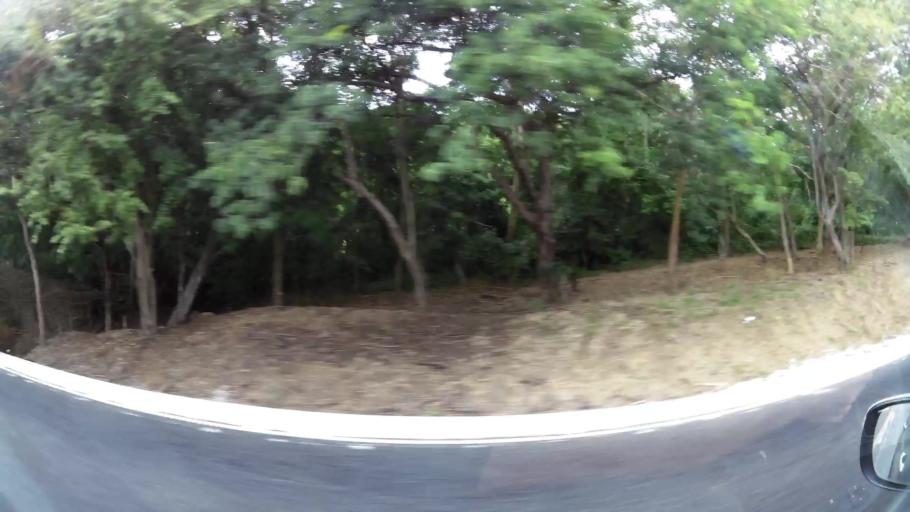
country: CR
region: Guanacaste
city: Nandayure
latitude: 10.2217
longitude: -85.2123
